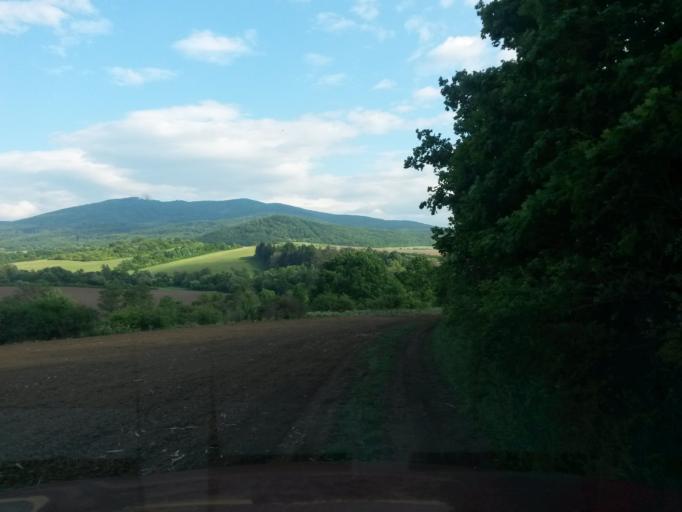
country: SK
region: Kosicky
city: Secovce
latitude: 48.7427
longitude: 21.4684
